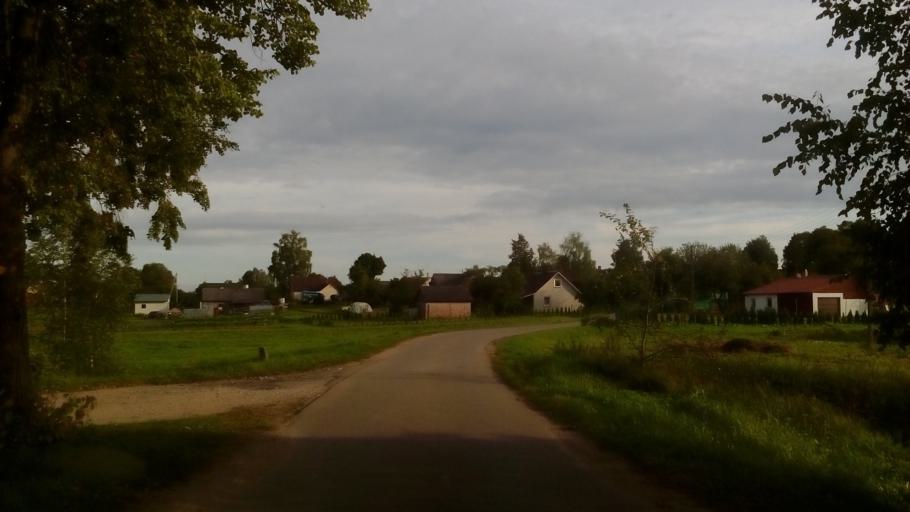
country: LT
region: Alytaus apskritis
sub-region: Alytus
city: Alytus
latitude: 54.3348
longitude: 23.8960
